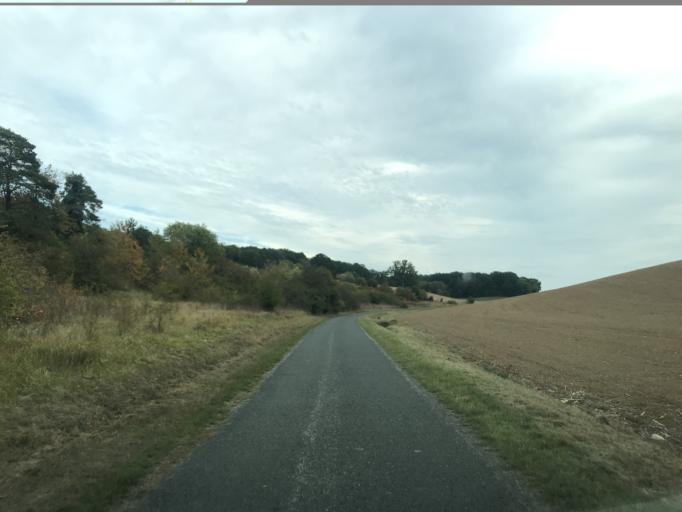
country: FR
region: Haute-Normandie
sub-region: Departement de l'Eure
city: Heudreville-sur-Eure
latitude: 49.0882
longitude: 1.2263
